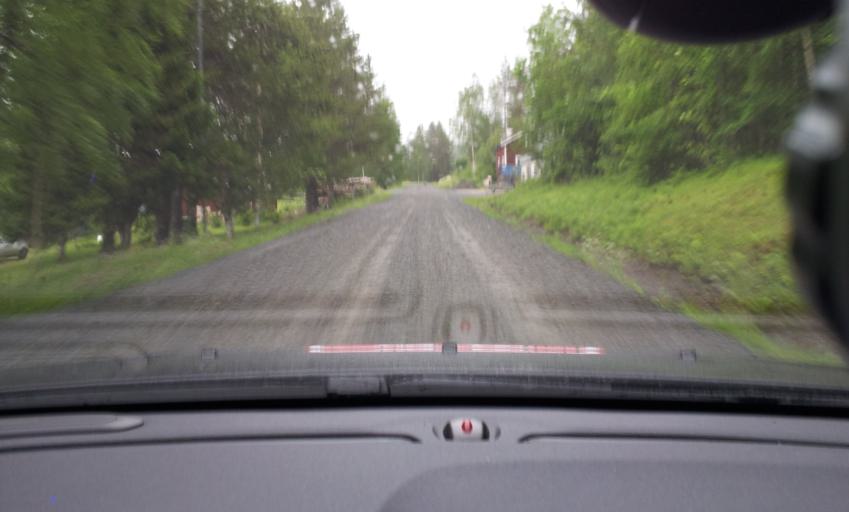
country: SE
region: Jaemtland
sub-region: Ragunda Kommun
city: Hammarstrand
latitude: 63.1331
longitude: 16.1191
